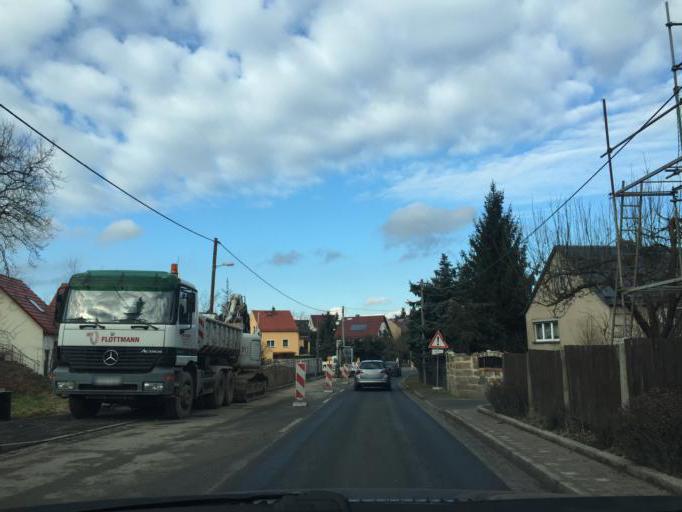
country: DE
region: Saxony
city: Radeburg
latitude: 51.1937
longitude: 13.7707
